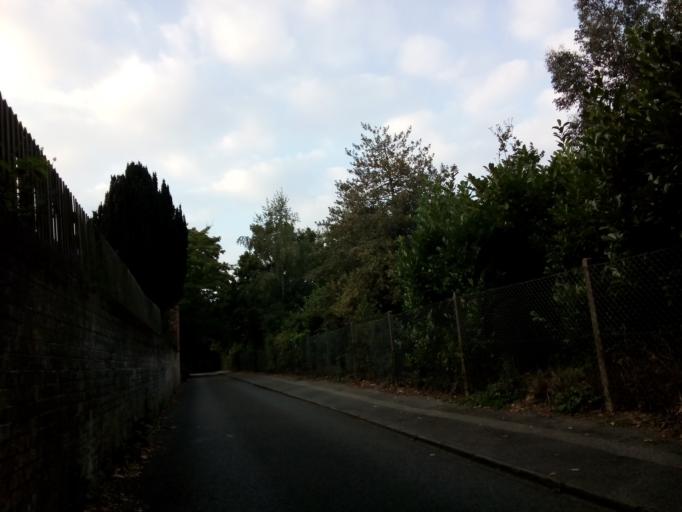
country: GB
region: England
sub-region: Suffolk
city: Ipswich
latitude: 52.0611
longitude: 1.1544
